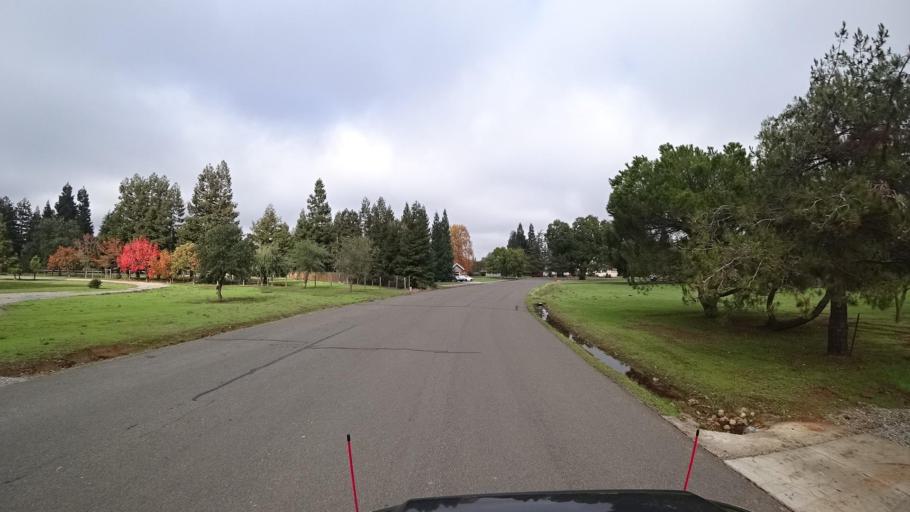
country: US
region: California
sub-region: Sacramento County
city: Vineyard
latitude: 38.4484
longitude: -121.3070
